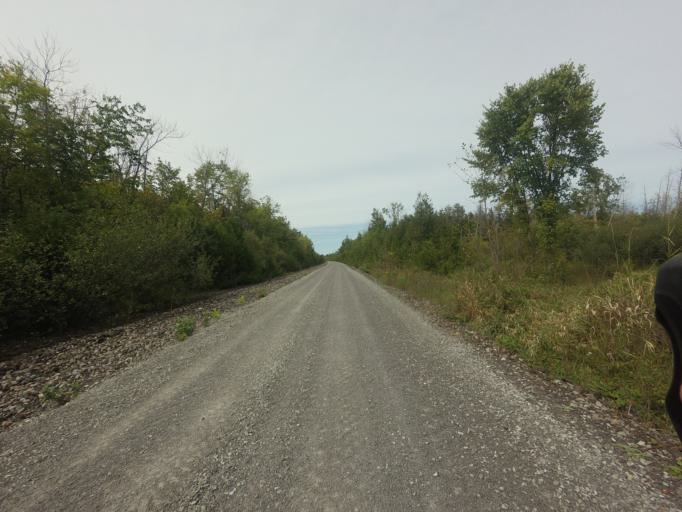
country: CA
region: Ontario
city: Carleton Place
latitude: 45.1210
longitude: -76.1268
